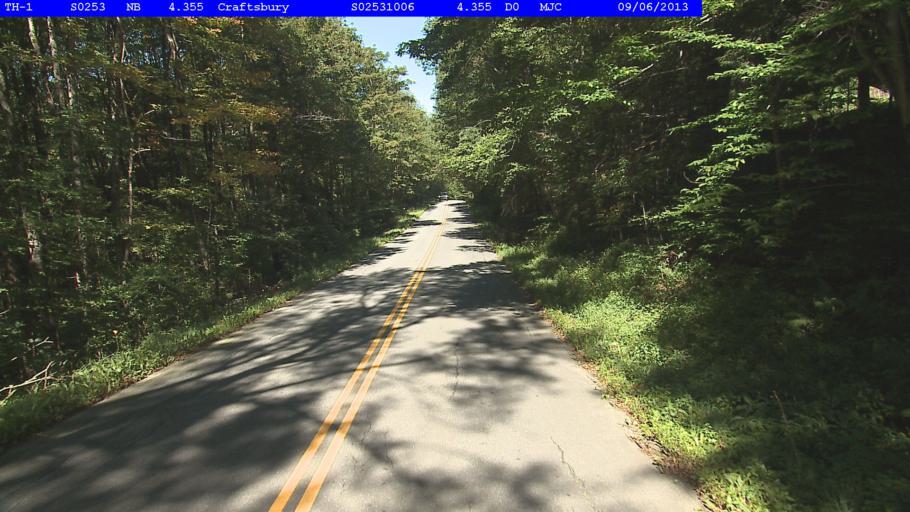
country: US
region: Vermont
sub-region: Caledonia County
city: Hardwick
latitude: 44.6684
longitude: -72.3897
